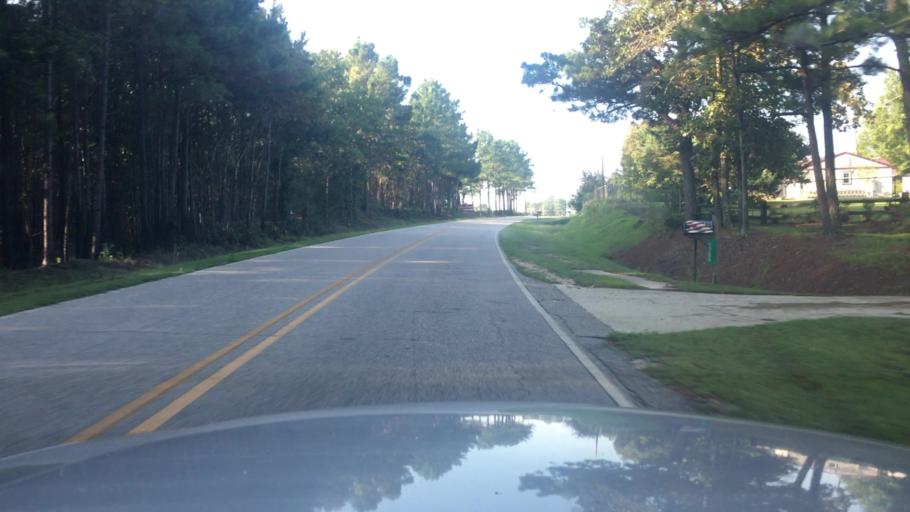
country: US
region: North Carolina
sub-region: Cumberland County
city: Spring Lake
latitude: 35.2169
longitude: -78.8940
